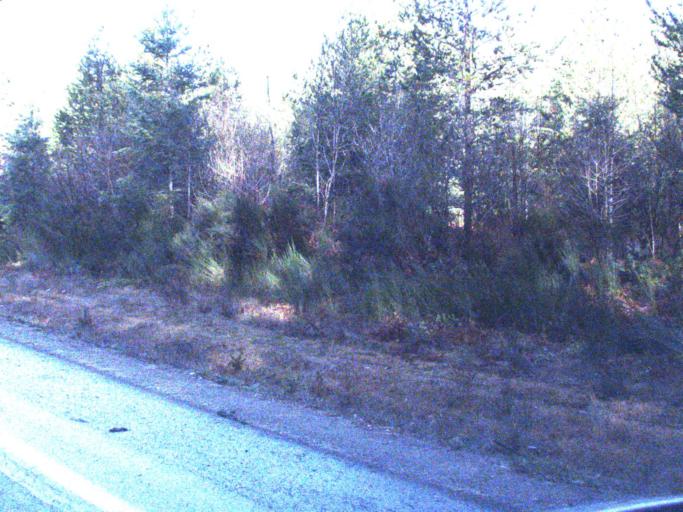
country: US
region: Washington
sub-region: Snohomish County
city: Darrington
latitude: 48.2662
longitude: -121.6393
